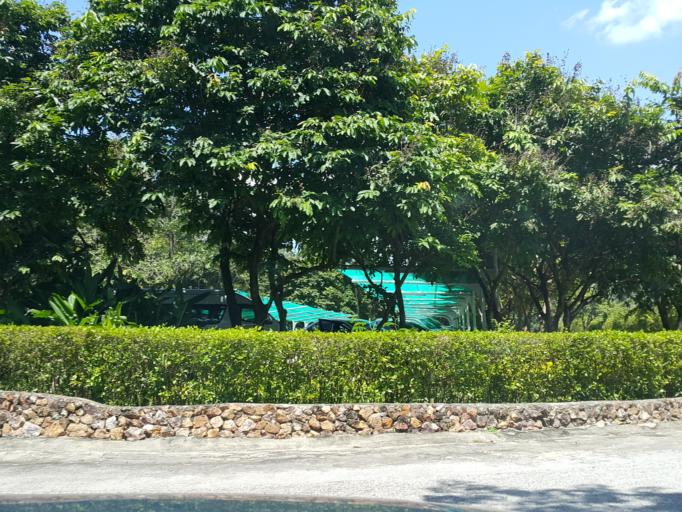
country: TH
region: Chiang Mai
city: San Kamphaeng
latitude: 18.6925
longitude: 99.1740
